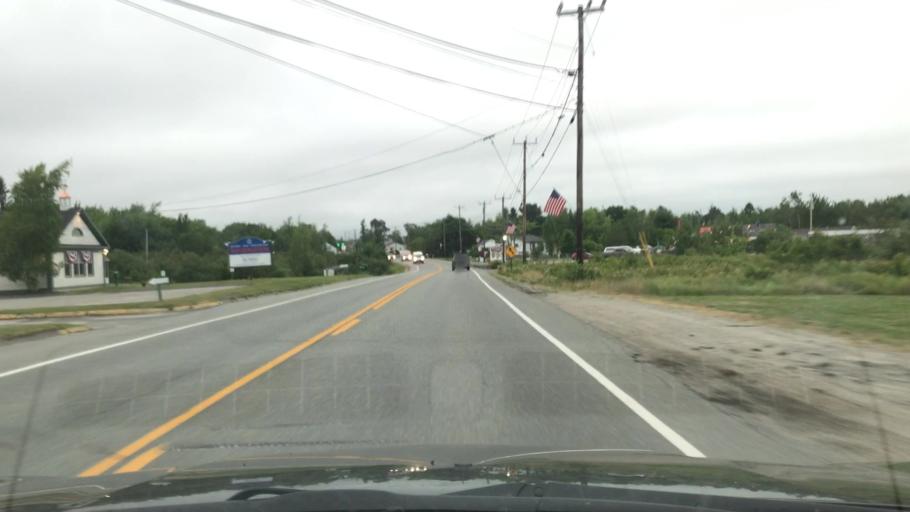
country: US
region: Maine
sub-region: Hancock County
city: Trenton
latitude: 44.4344
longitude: -68.3689
